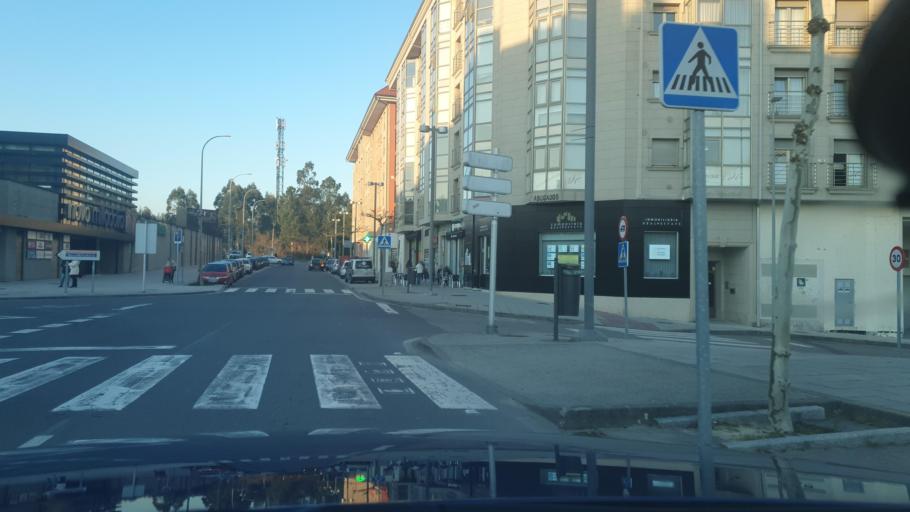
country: ES
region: Galicia
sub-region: Provincia da Coruna
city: Santiago de Compostela
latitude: 42.8472
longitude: -8.5803
